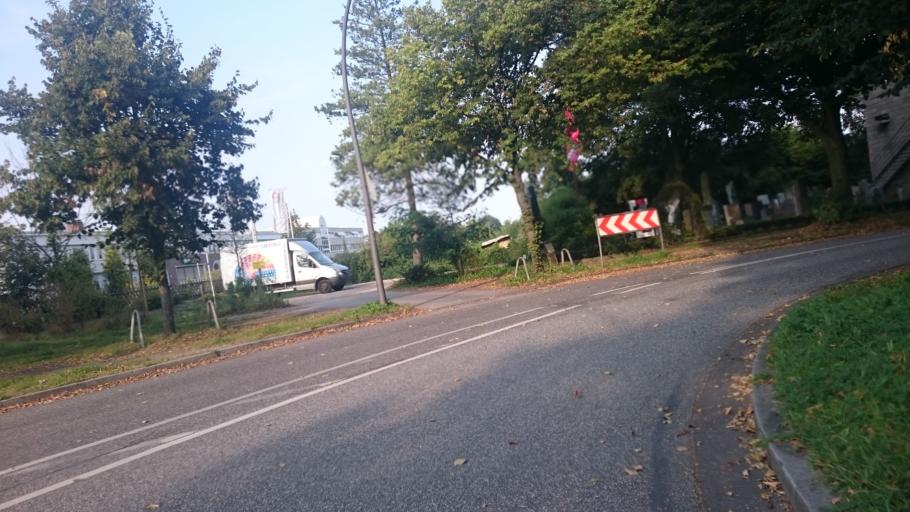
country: DE
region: Hamburg
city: Stellingen
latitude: 53.5706
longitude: 9.9235
